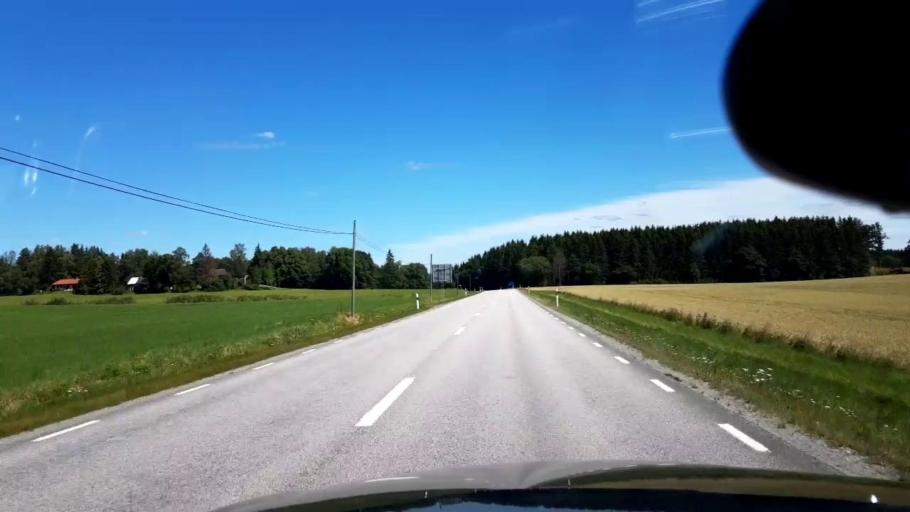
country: SE
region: Uppsala
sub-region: Habo Kommun
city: Balsta
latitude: 59.6324
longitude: 17.6013
